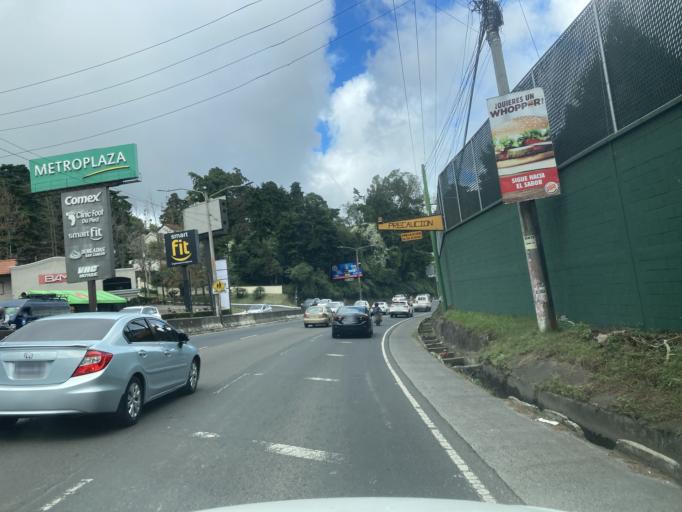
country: GT
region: Guatemala
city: Santa Catarina Pinula
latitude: 14.5676
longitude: -90.4716
